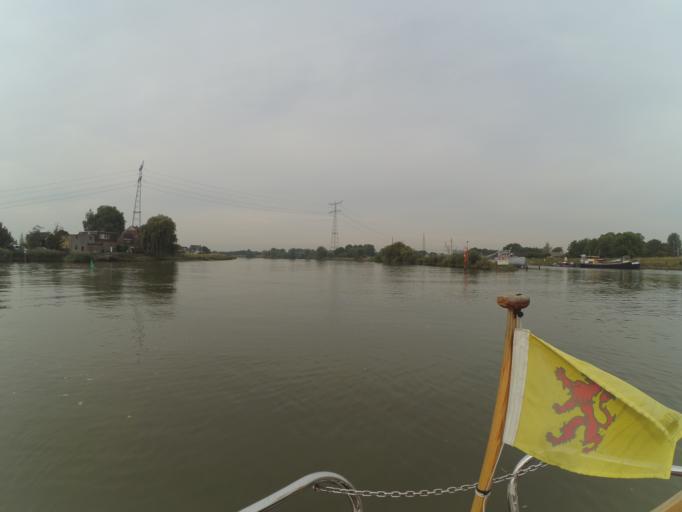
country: NL
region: South Holland
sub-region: Gemeente Krimpen aan den IJssel
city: Krimpen aan den IJssel
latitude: 51.9365
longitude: 4.6278
